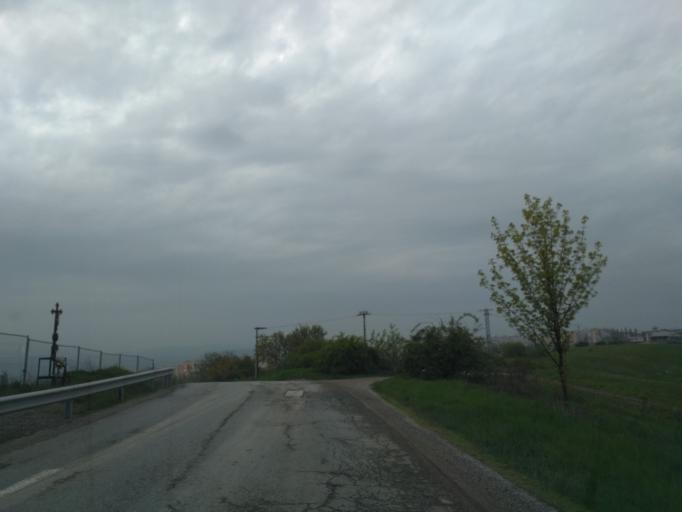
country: SK
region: Kosicky
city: Kosice
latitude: 48.7223
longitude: 21.2958
